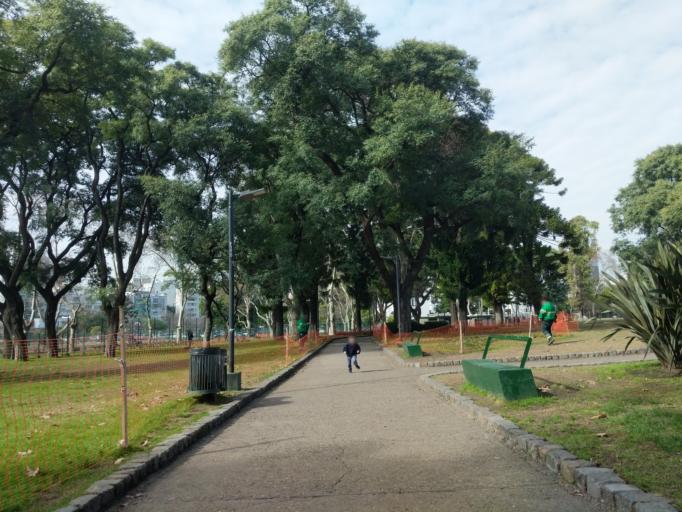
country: AR
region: Buenos Aires F.D.
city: Colegiales
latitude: -34.6058
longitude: -58.4354
